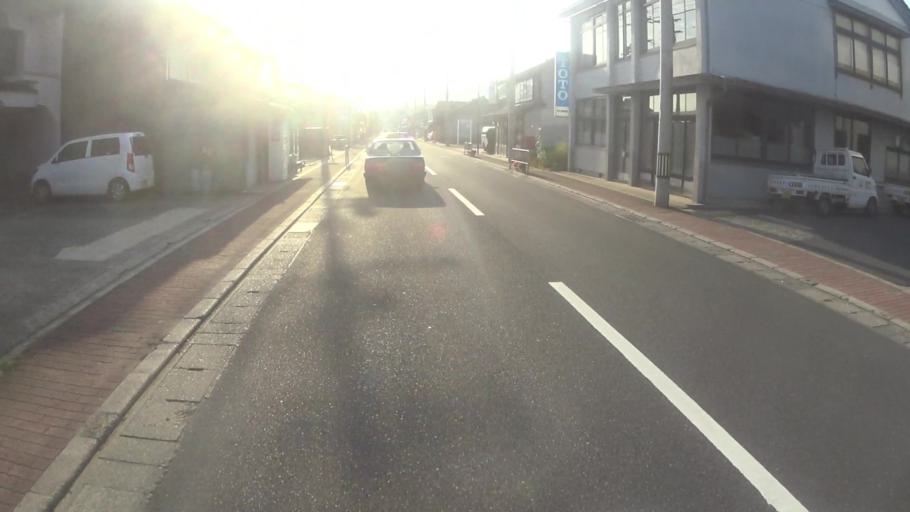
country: JP
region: Kyoto
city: Miyazu
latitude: 35.6264
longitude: 135.0646
